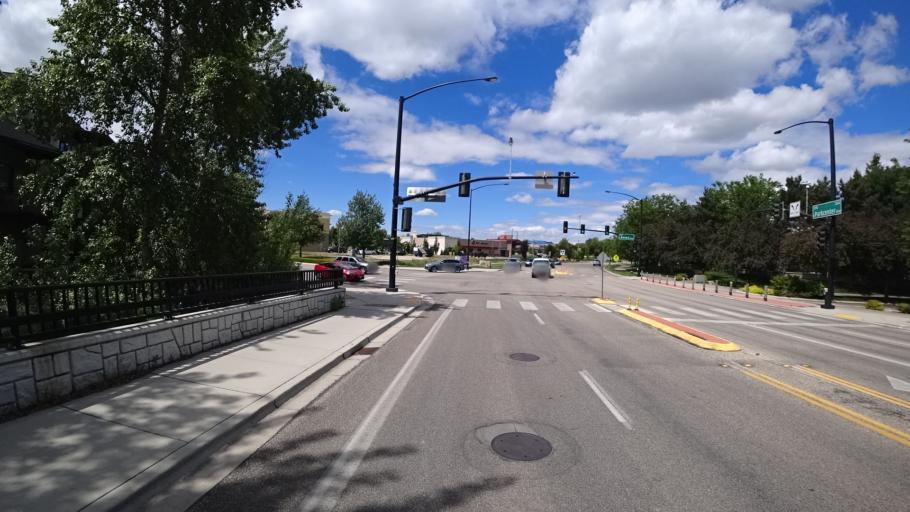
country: US
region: Idaho
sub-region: Ada County
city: Boise
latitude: 43.5753
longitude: -116.1538
